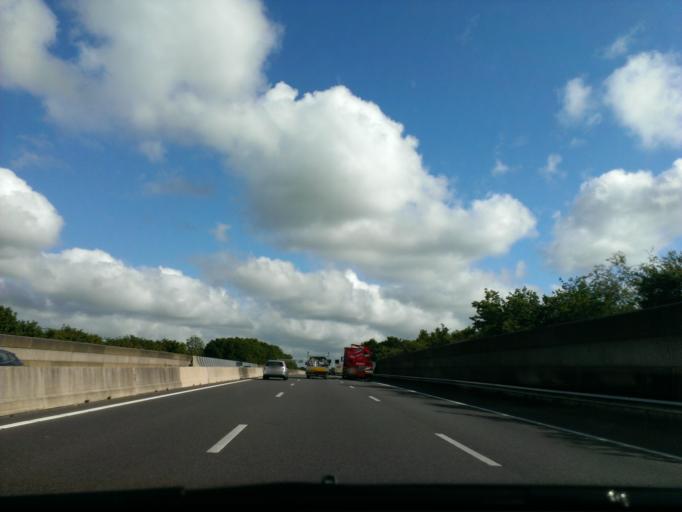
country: NL
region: Overijssel
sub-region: Gemeente Staphorst
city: Staphorst
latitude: 52.6420
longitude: 6.2024
